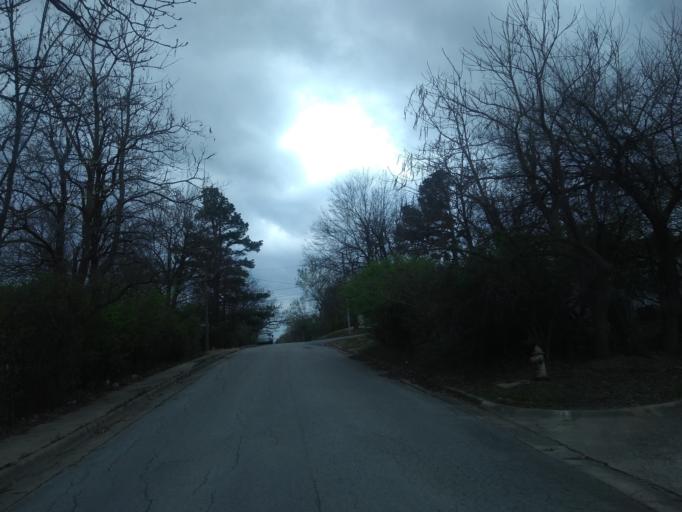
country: US
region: Arkansas
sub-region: Washington County
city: Fayetteville
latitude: 36.0773
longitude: -94.1721
